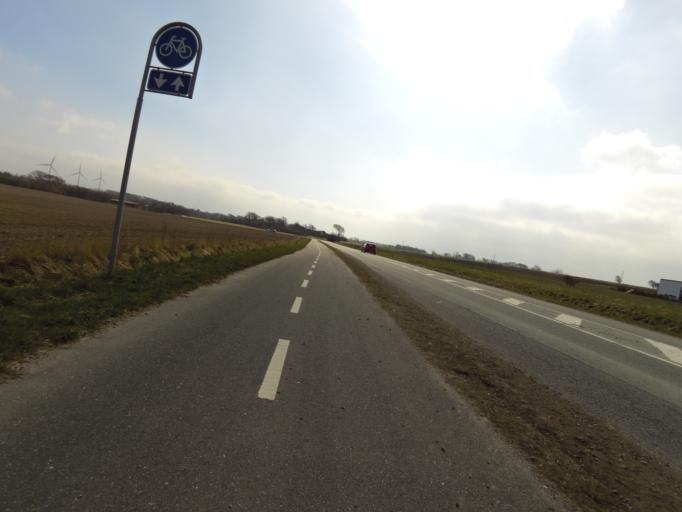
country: DK
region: Central Jutland
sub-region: Struer Kommune
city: Struer
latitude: 56.4734
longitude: 8.6061
